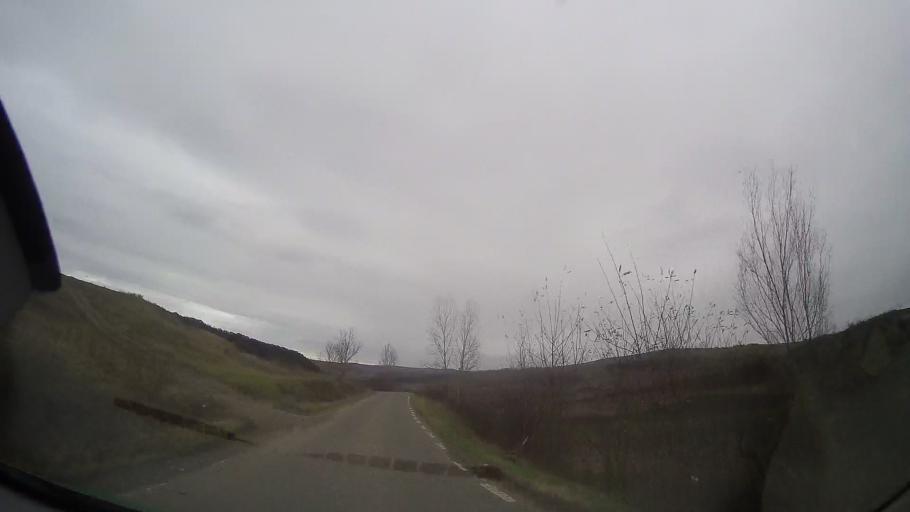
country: RO
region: Mures
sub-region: Comuna Bala
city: Bala
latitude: 46.7138
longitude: 24.5156
